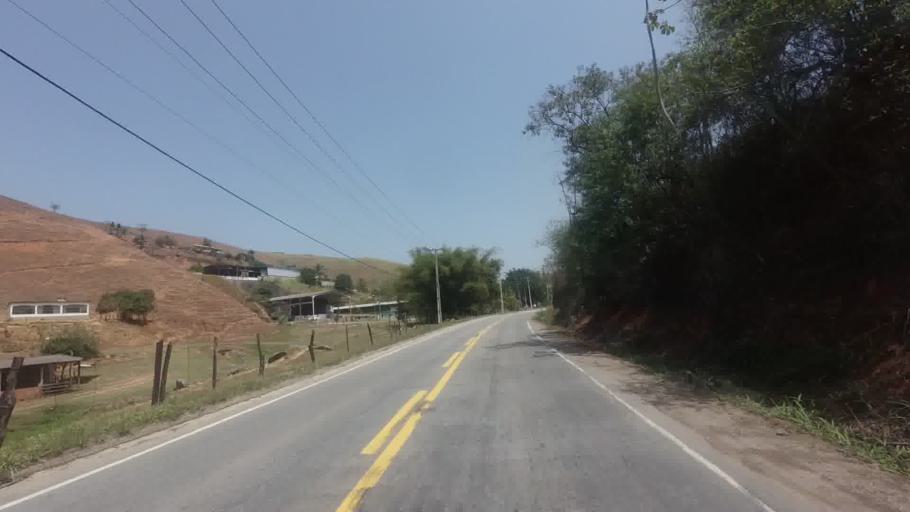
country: BR
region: Espirito Santo
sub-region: Cachoeiro De Itapemirim
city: Cachoeiro de Itapemirim
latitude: -20.8574
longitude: -41.0729
